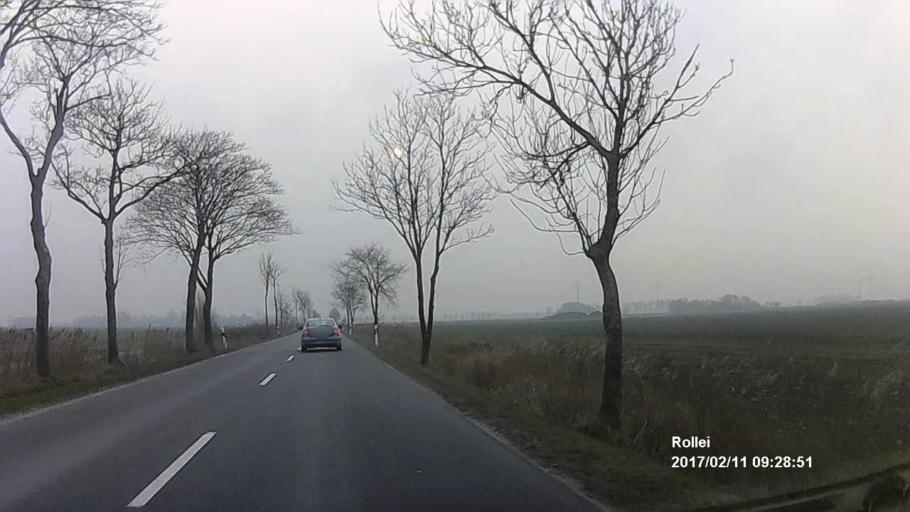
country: DE
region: Lower Saxony
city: Hinte
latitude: 53.4426
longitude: 7.1555
